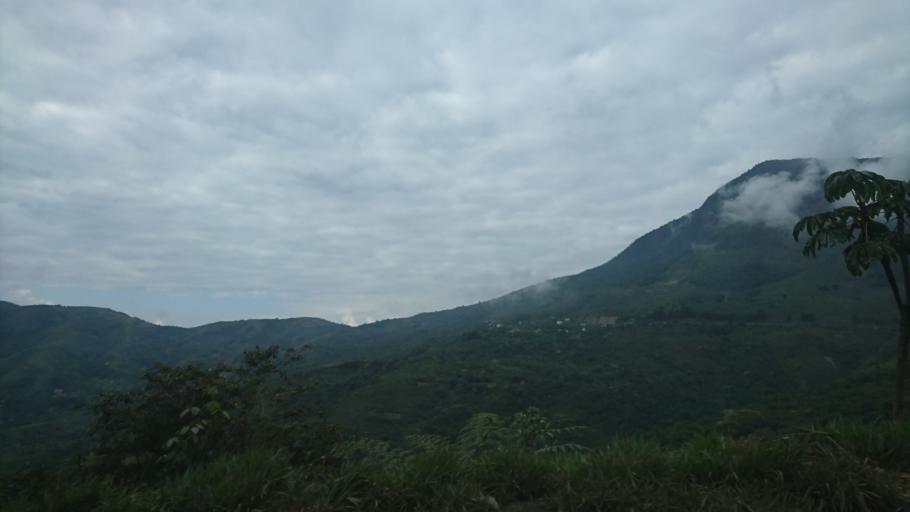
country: BO
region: La Paz
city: Coroico
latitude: -16.2246
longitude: -67.6764
